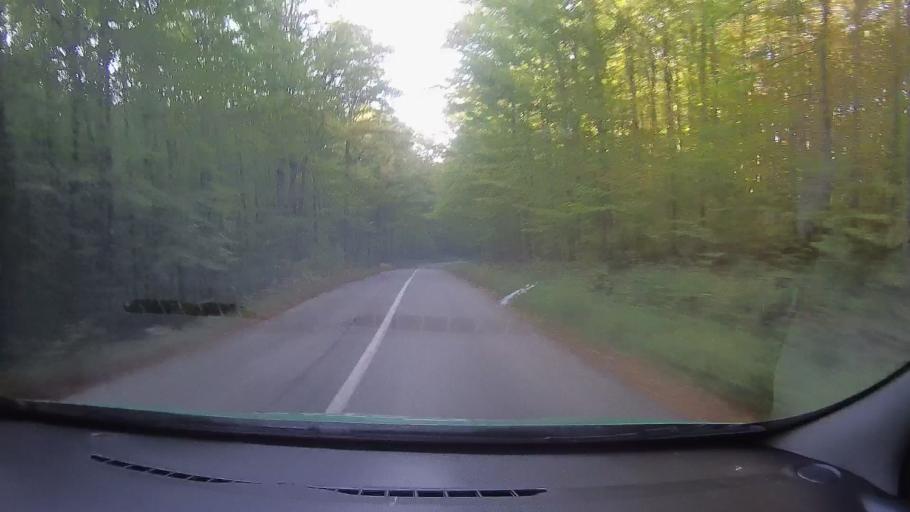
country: RO
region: Timis
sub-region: Comuna Nadrag
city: Nadrag
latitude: 45.6777
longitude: 22.1596
